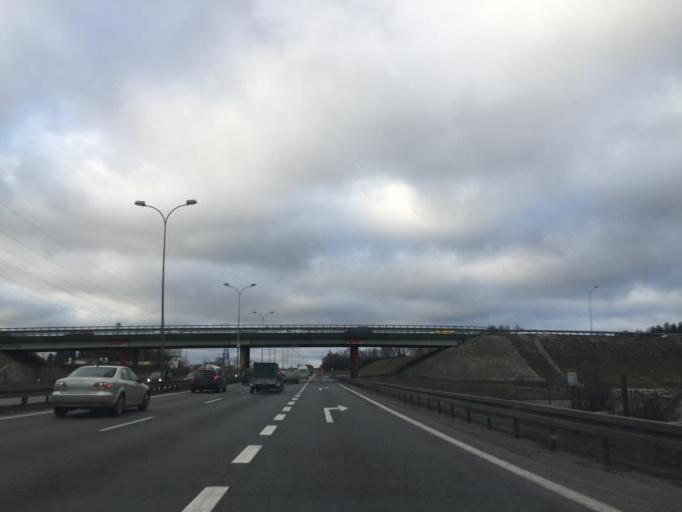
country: PL
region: Pomeranian Voivodeship
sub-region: Gdynia
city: Wielki Kack
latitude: 54.4107
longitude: 18.4863
